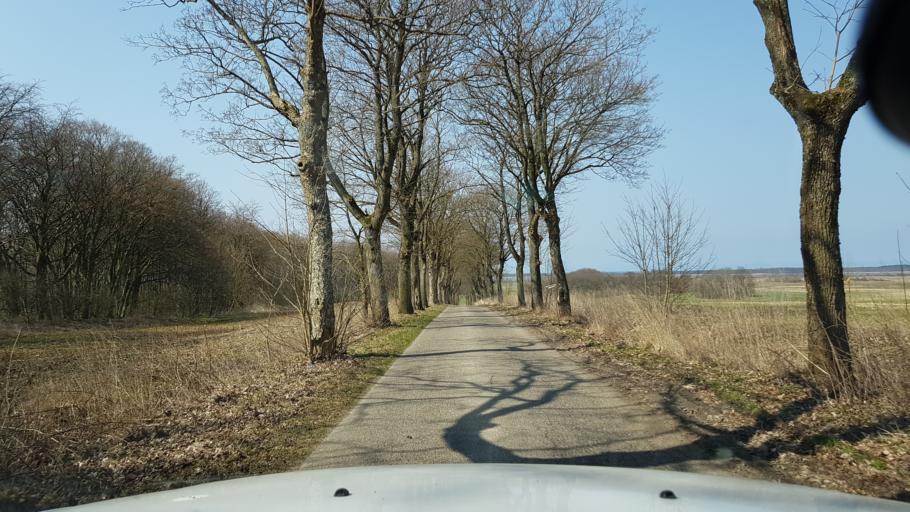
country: PL
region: West Pomeranian Voivodeship
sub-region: Powiat slawienski
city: Darlowo
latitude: 54.4667
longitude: 16.4956
